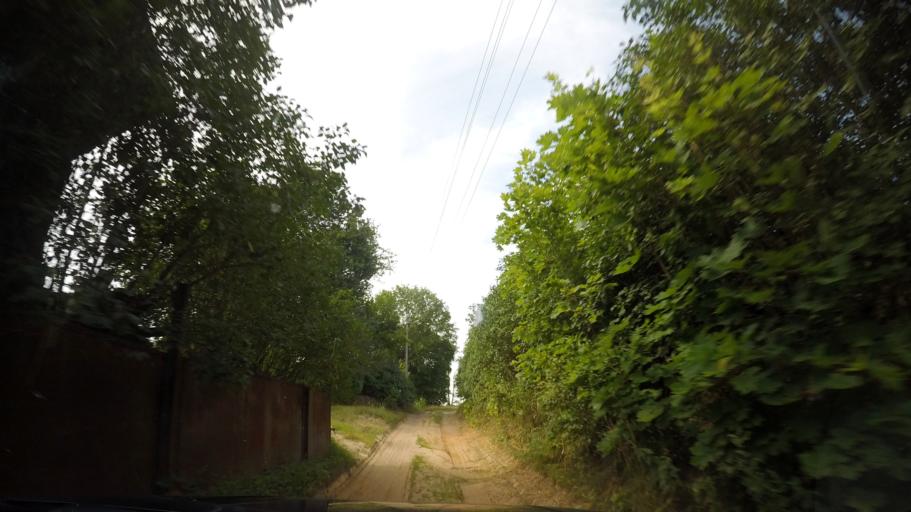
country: BY
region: Grodnenskaya
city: Skidal'
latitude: 53.8383
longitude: 24.1894
